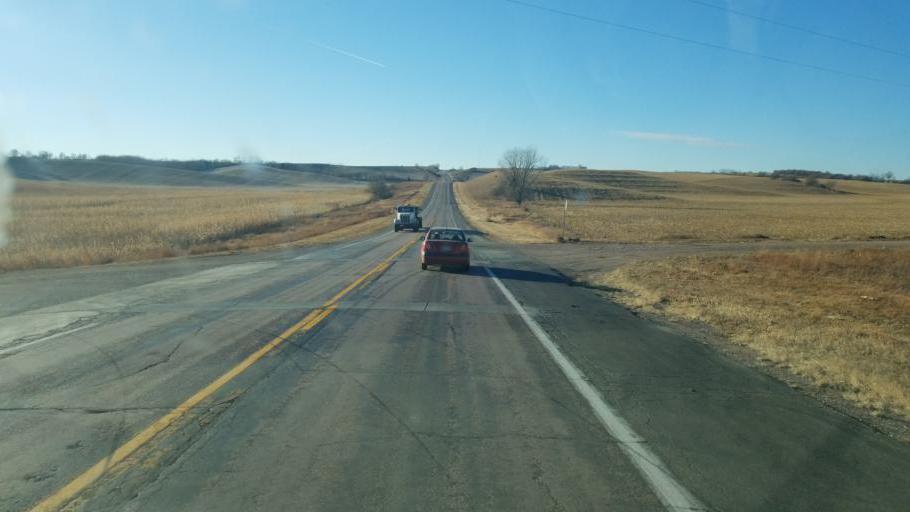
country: US
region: Nebraska
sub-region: Dixon County
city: Ponca
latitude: 42.4739
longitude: -96.7065
